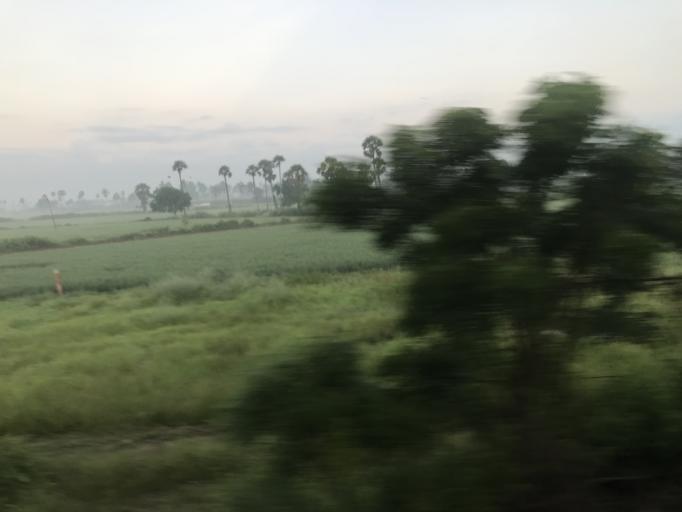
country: IN
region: Andhra Pradesh
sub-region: Guntur
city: Ponnur
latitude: 16.1059
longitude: 80.5747
